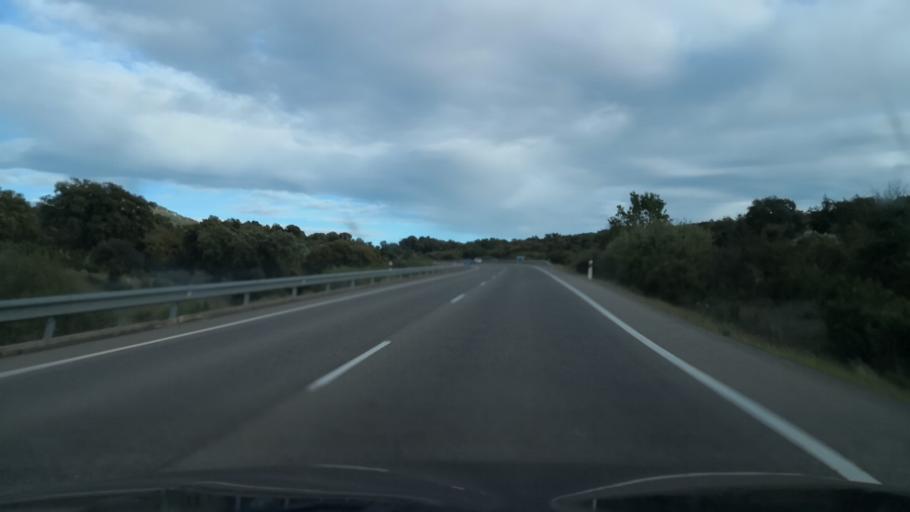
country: ES
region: Extremadura
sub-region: Provincia de Caceres
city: Pedroso de Acim
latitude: 39.8288
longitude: -6.3802
